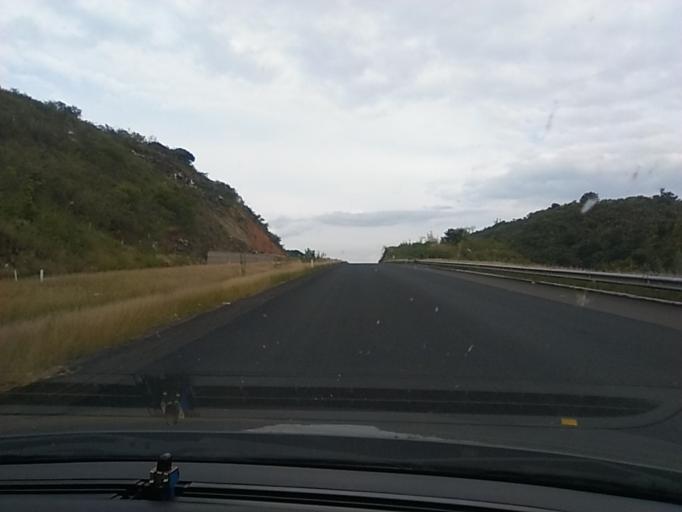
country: MX
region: Mexico
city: Huaniqueo de Morales
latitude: 19.8854
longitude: -101.4524
